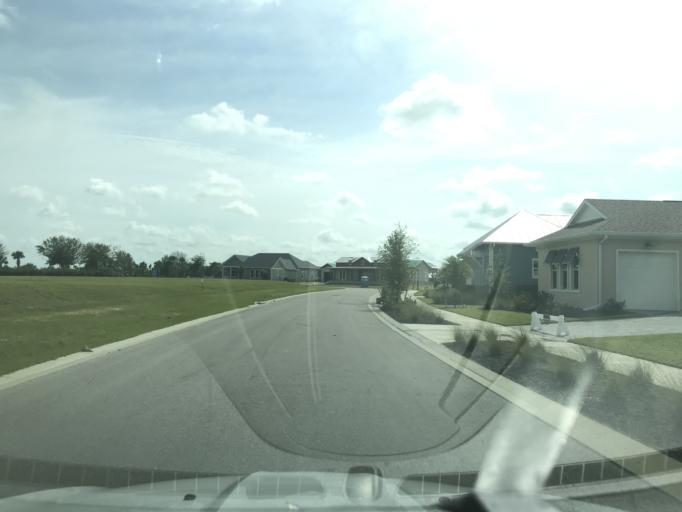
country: US
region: Florida
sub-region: Lee County
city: Fort Myers Shores
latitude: 26.7811
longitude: -81.7518
